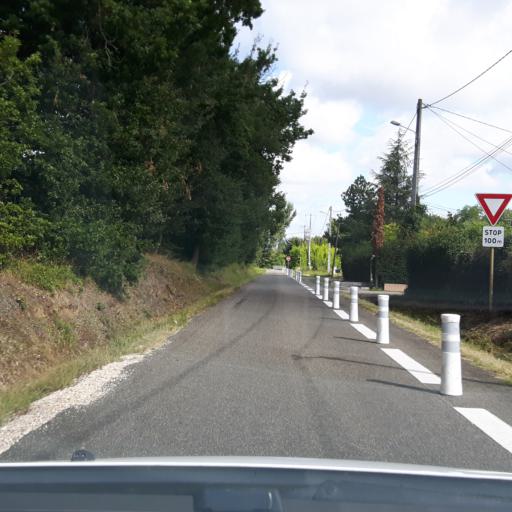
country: FR
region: Midi-Pyrenees
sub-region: Departement de la Haute-Garonne
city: Bouloc
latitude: 43.7916
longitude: 1.4075
